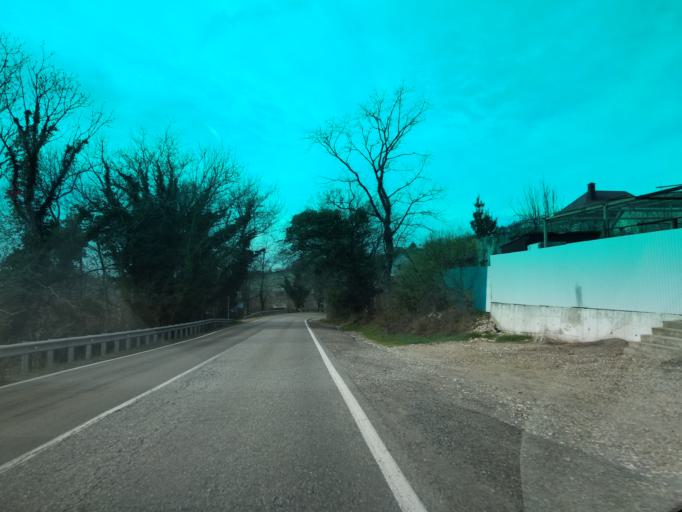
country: RU
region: Krasnodarskiy
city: Shepsi
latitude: 44.0850
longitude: 39.1297
